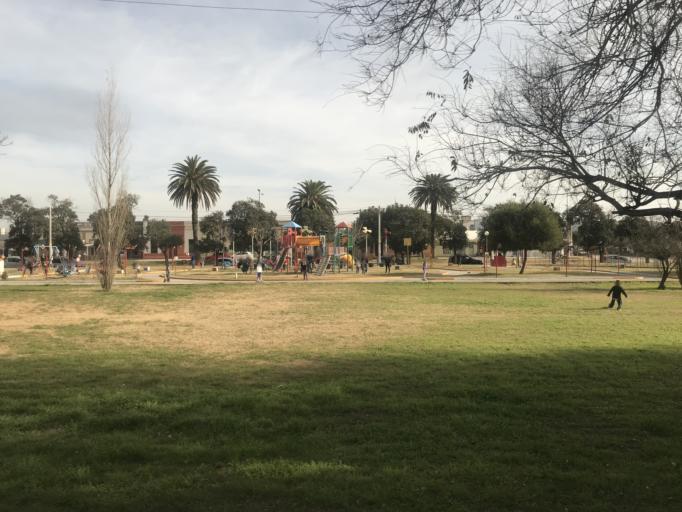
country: AR
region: Cordoba
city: Laguna Larga
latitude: -31.7767
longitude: -63.8033
